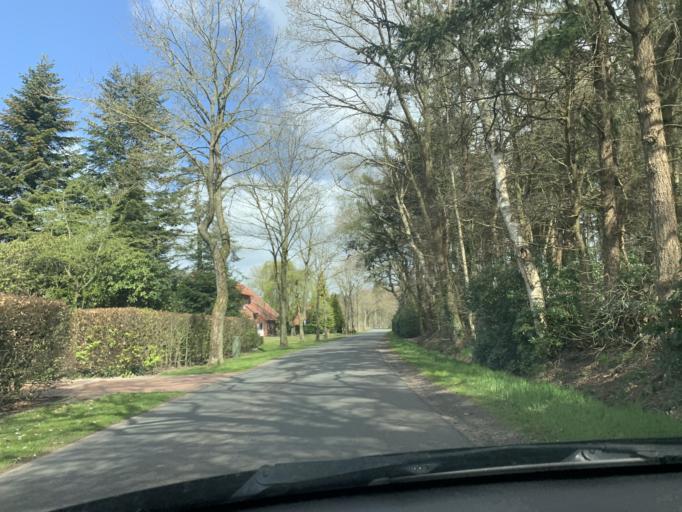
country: DE
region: Lower Saxony
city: Westerstede
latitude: 53.2842
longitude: 7.9460
